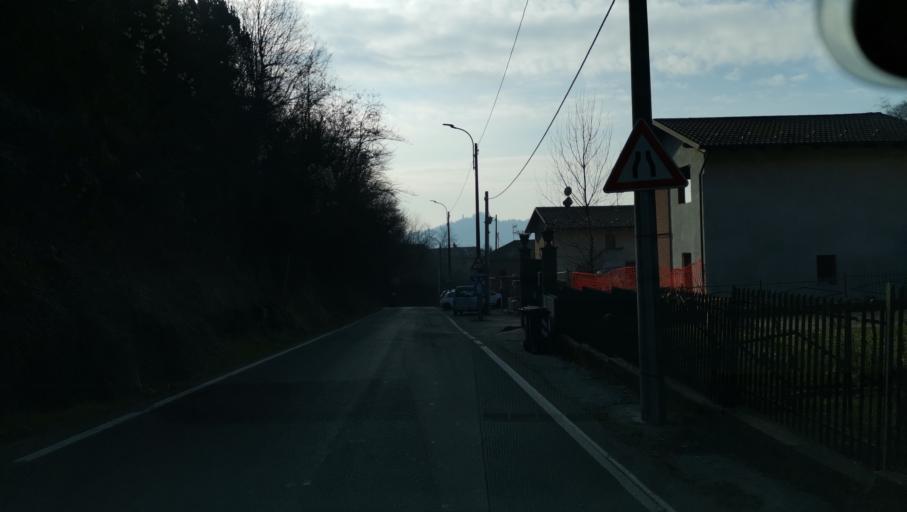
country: IT
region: Piedmont
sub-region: Provincia di Torino
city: Rivalba
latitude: 45.1182
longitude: 7.8889
